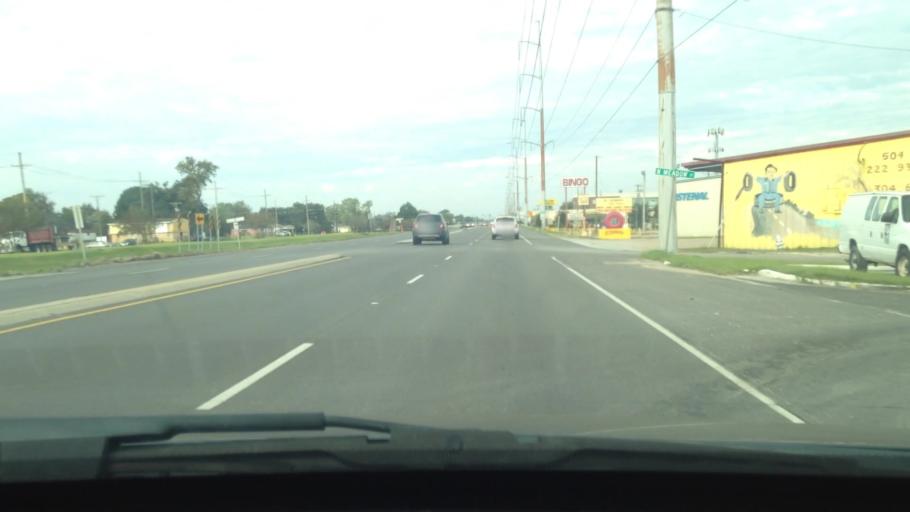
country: US
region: Louisiana
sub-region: Jefferson Parish
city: River Ridge
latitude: 29.9781
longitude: -90.2146
